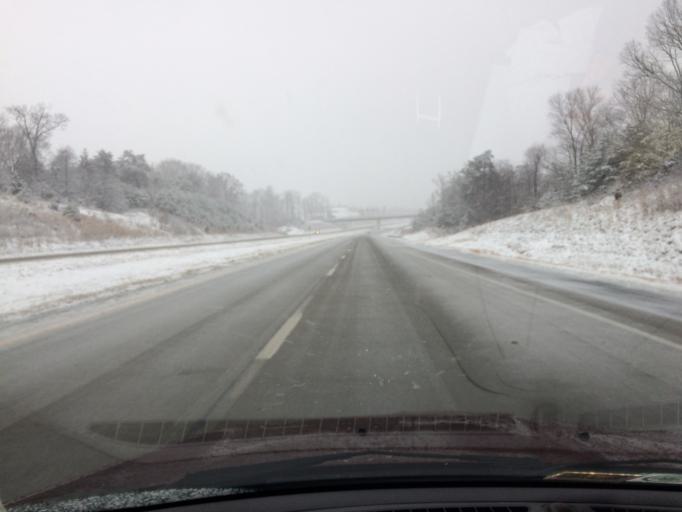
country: US
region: Virginia
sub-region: Amherst County
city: Madison Heights
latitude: 37.4679
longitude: -79.0828
